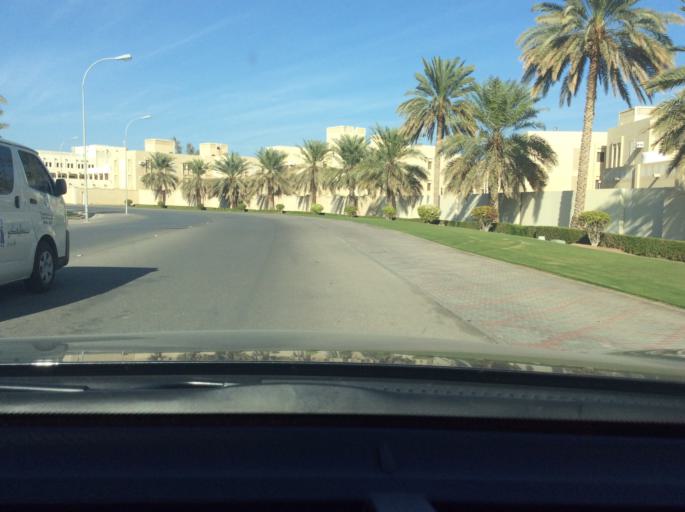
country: OM
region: Muhafazat Masqat
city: As Sib al Jadidah
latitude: 23.5839
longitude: 58.1710
